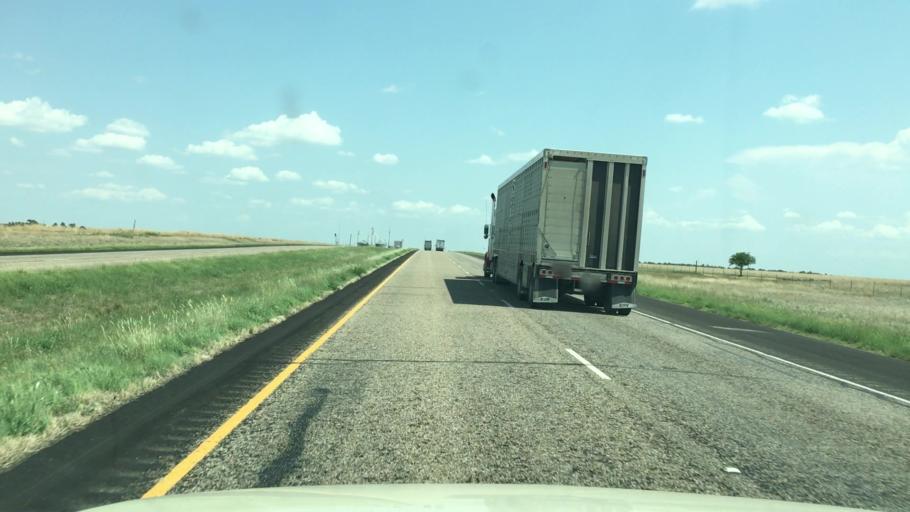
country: US
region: Texas
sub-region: Armstrong County
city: Claude
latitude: 35.1244
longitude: -101.3944
